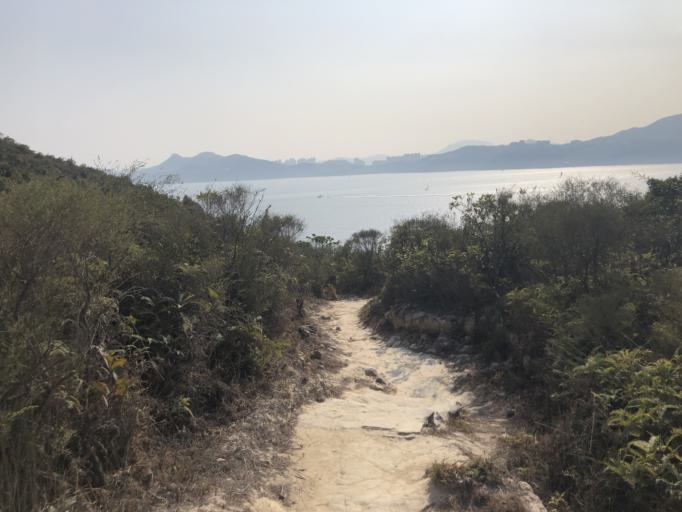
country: HK
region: Sai Kung
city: Sai Kung
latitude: 22.3630
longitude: 114.2934
